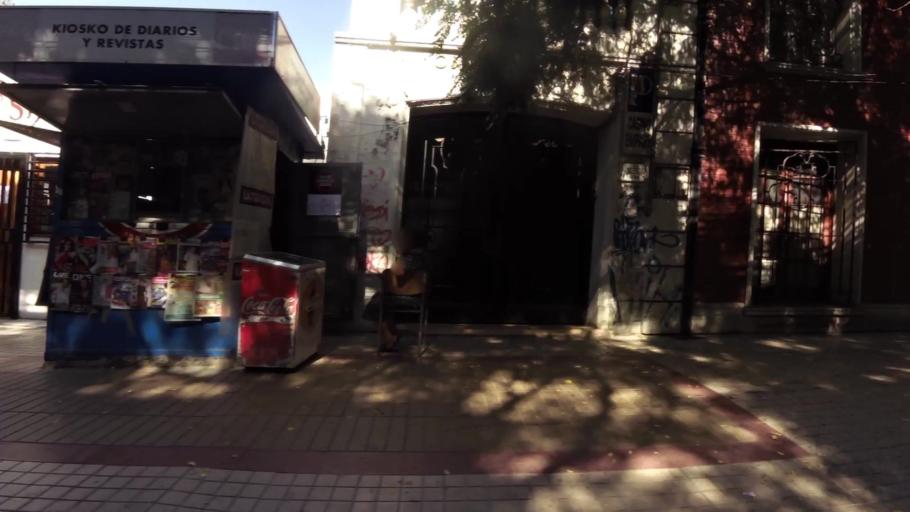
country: CL
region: Maule
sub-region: Provincia de Talca
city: Talca
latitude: -35.4249
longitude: -71.6651
